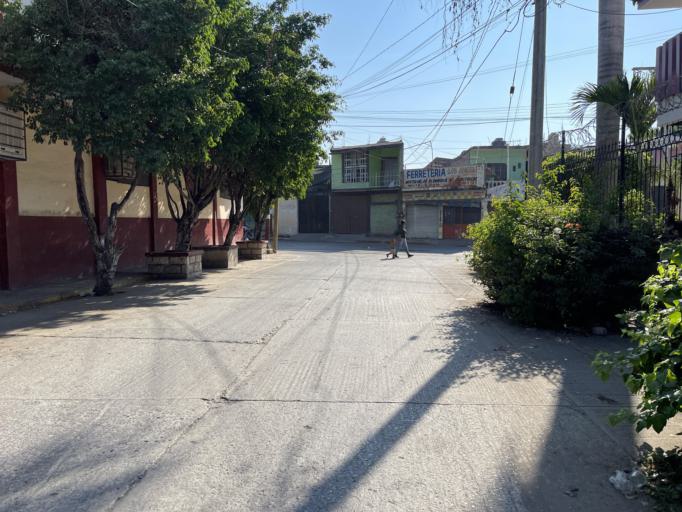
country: MX
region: Guerrero
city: Iguala de la Independencia
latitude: 18.3410
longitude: -99.5471
